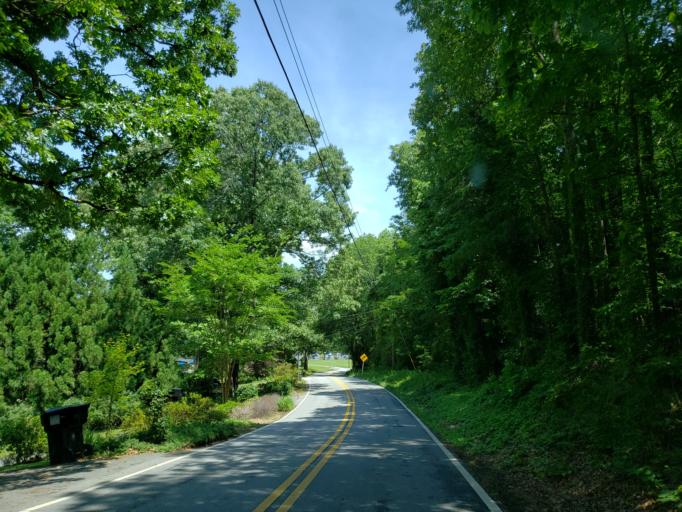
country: US
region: Georgia
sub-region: Paulding County
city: Hiram
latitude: 33.9022
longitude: -84.7656
